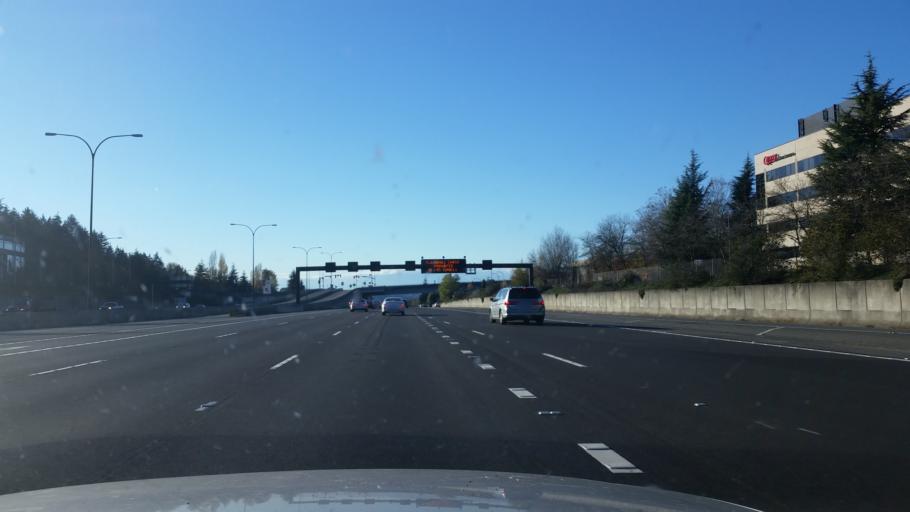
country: US
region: Washington
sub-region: King County
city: Eastgate
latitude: 47.5794
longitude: -122.1458
